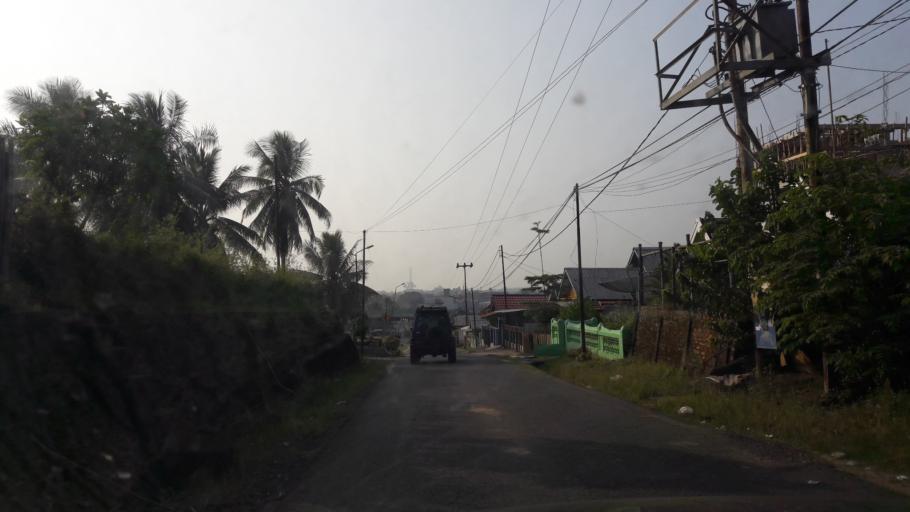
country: ID
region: South Sumatra
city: Gunungmegang Dalam
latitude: -3.2681
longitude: 103.8190
